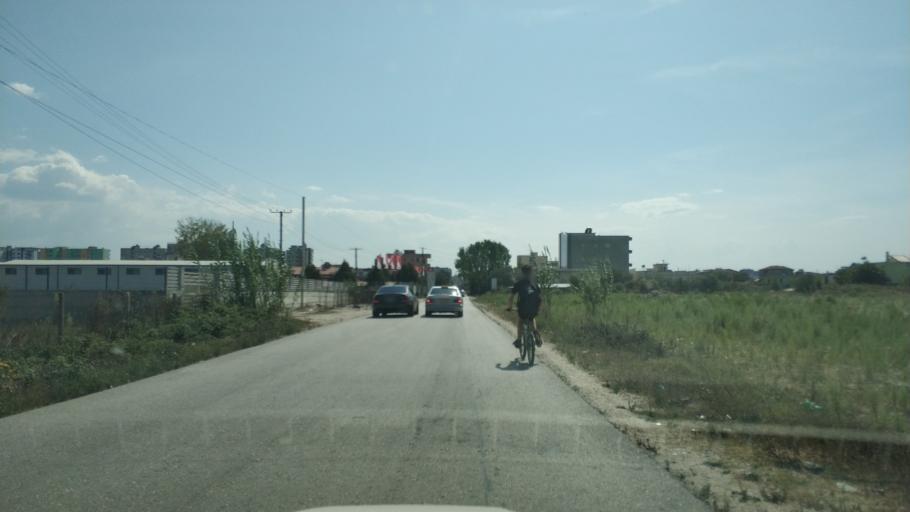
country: AL
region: Fier
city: Fier
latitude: 40.7402
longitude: 19.5596
